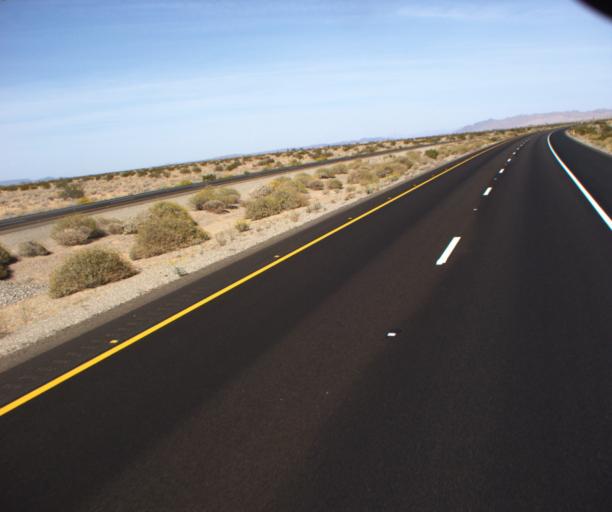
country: US
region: Arizona
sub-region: Yuma County
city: Fortuna Foothills
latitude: 32.6011
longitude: -114.5395
